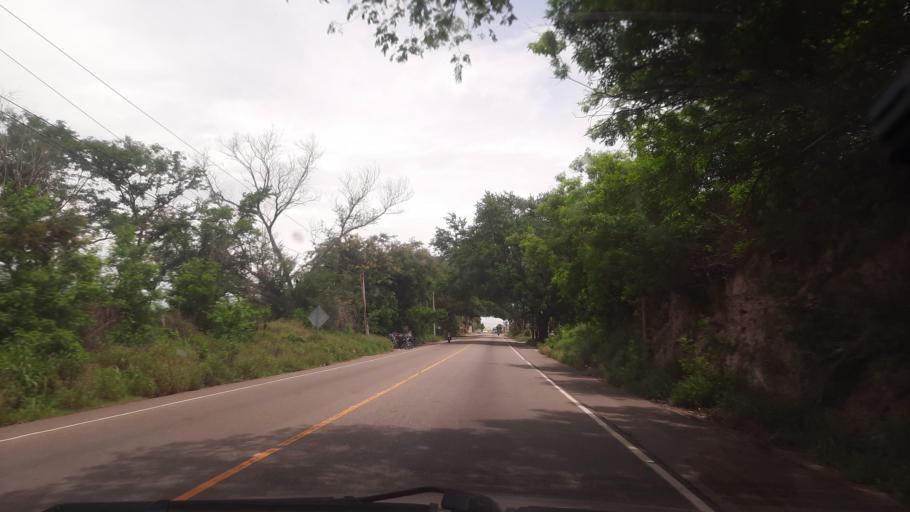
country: GT
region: Zacapa
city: Rio Hondo
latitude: 15.0515
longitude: -89.5636
